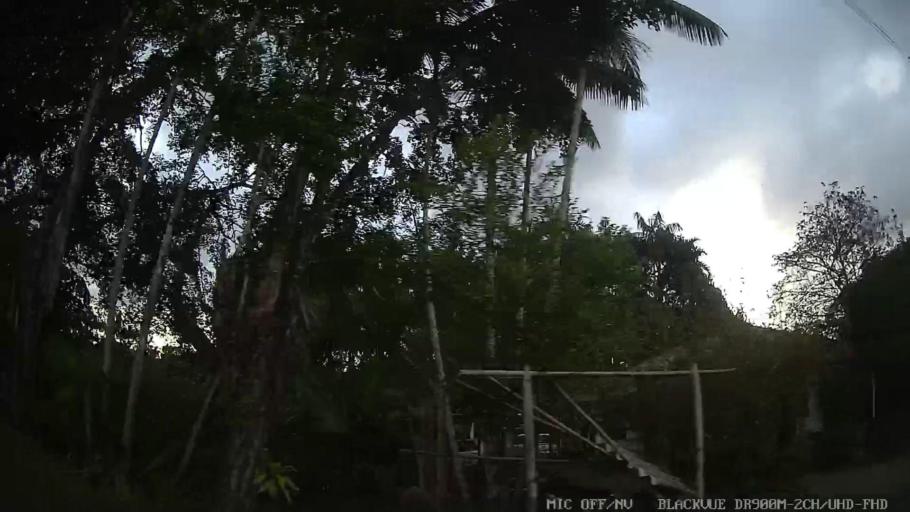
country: BR
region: Sao Paulo
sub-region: Itanhaem
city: Itanhaem
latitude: -24.0884
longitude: -46.7974
